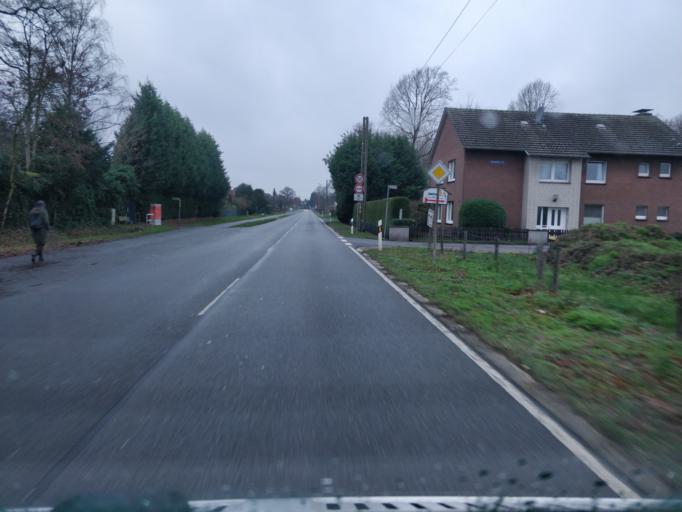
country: DE
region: North Rhine-Westphalia
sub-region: Regierungsbezirk Dusseldorf
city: Mehrhoog
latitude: 51.7417
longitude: 6.5296
